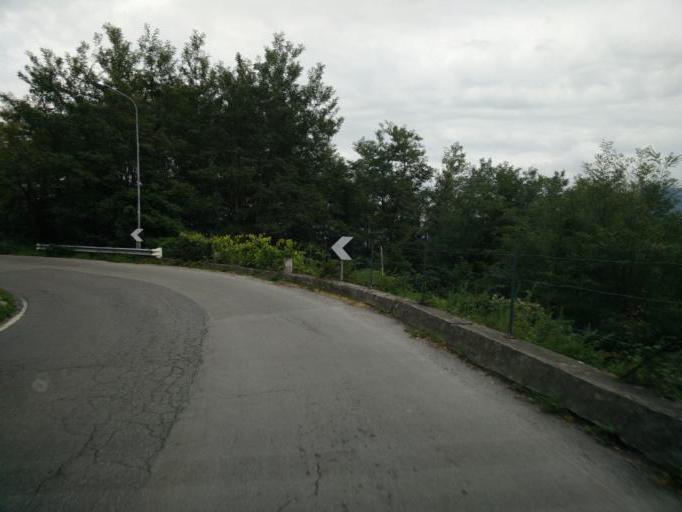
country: IT
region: Tuscany
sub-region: Provincia di Lucca
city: San Romano
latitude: 44.1716
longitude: 10.3377
